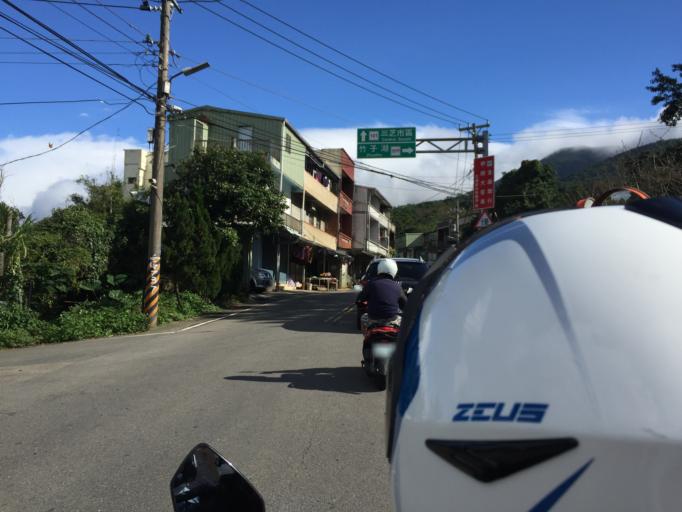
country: TW
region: Taipei
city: Taipei
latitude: 25.2049
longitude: 121.5007
